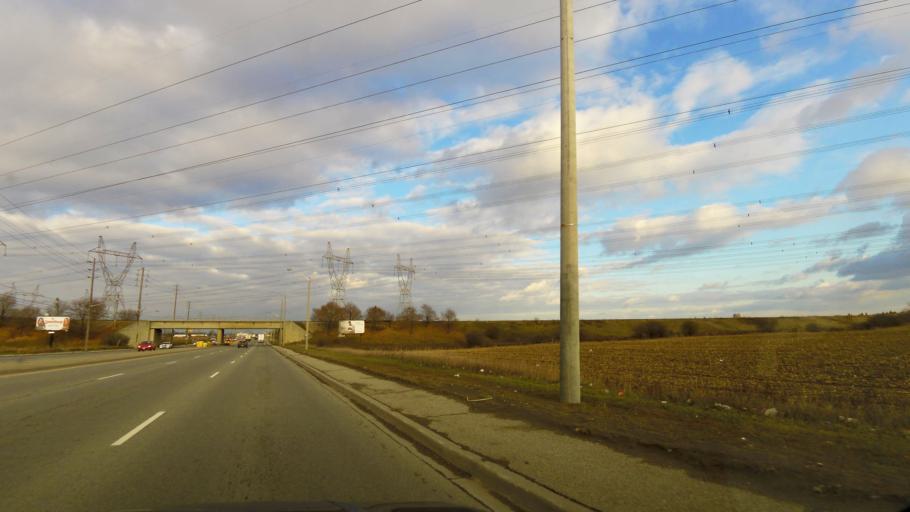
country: CA
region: Ontario
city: Brampton
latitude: 43.7275
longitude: -79.6645
